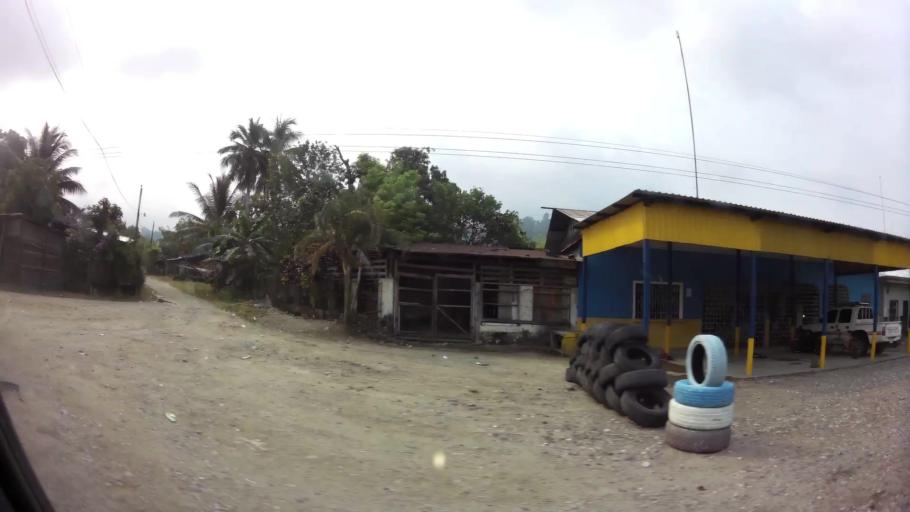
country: HN
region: Yoro
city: Toyos
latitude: 15.5243
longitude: -87.6575
